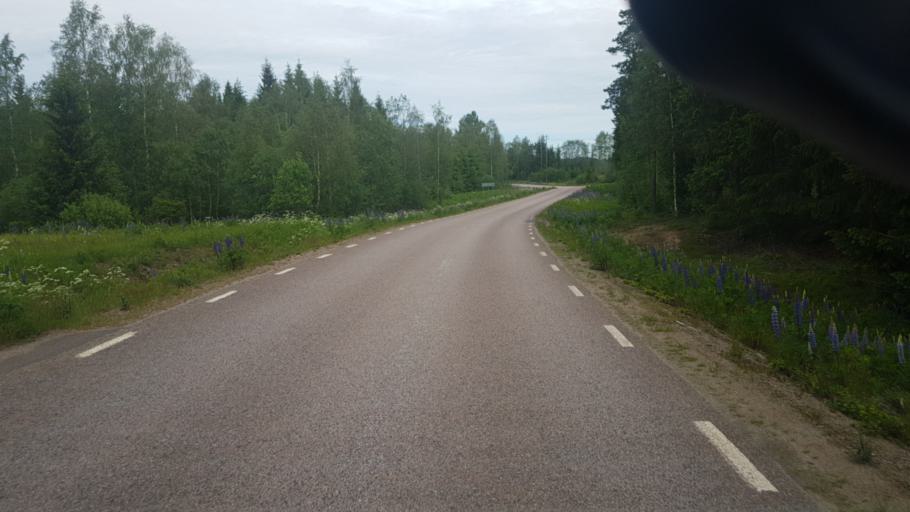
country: SE
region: Vaermland
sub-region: Arvika Kommun
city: Arvika
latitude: 59.7549
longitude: 12.8235
